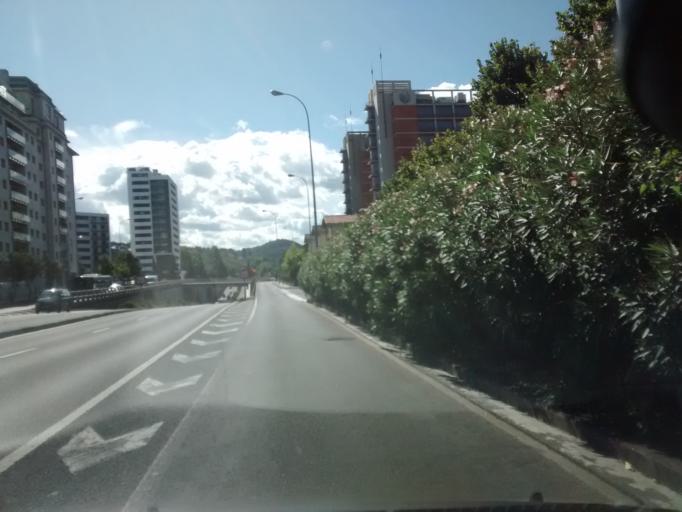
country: ES
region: Basque Country
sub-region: Provincia de Guipuzcoa
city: San Sebastian
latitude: 43.3030
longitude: -2.0047
